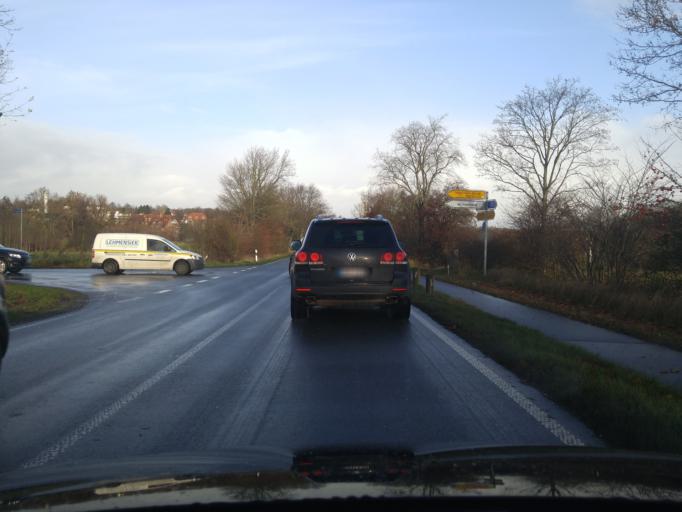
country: DE
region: Schleswig-Holstein
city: Timmendorfer Strand
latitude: 53.9872
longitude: 10.7731
